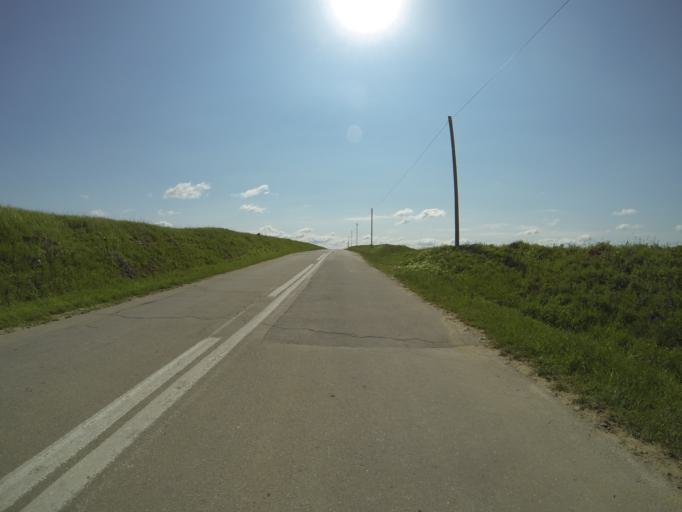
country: RO
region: Dolj
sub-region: Comuna Orodelu
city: Orodelu
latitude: 44.2395
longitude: 23.2127
